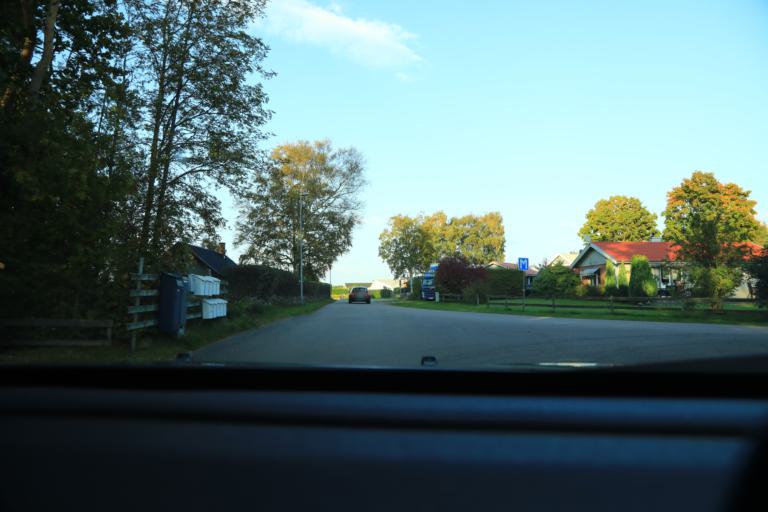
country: SE
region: Halland
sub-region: Varbergs Kommun
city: Traslovslage
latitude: 57.0470
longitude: 12.2936
